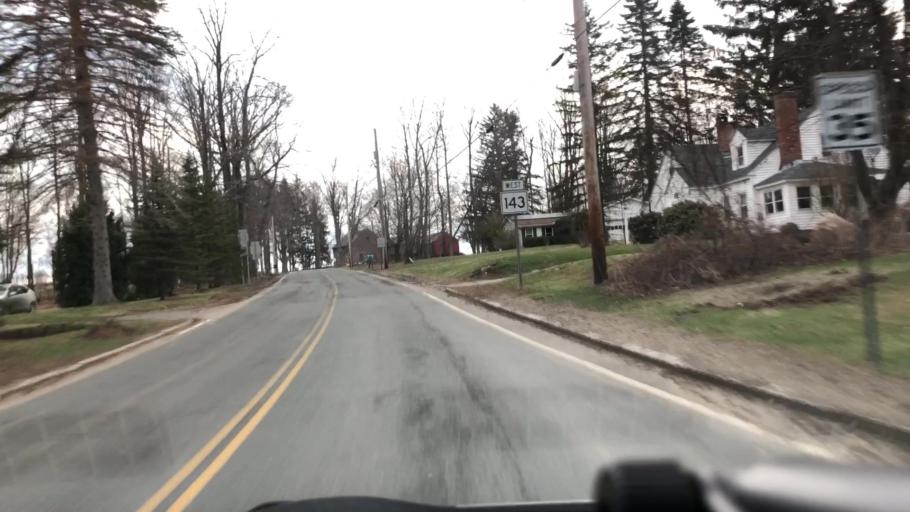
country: US
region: Massachusetts
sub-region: Hampshire County
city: Chesterfield
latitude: 42.4106
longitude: -72.9368
